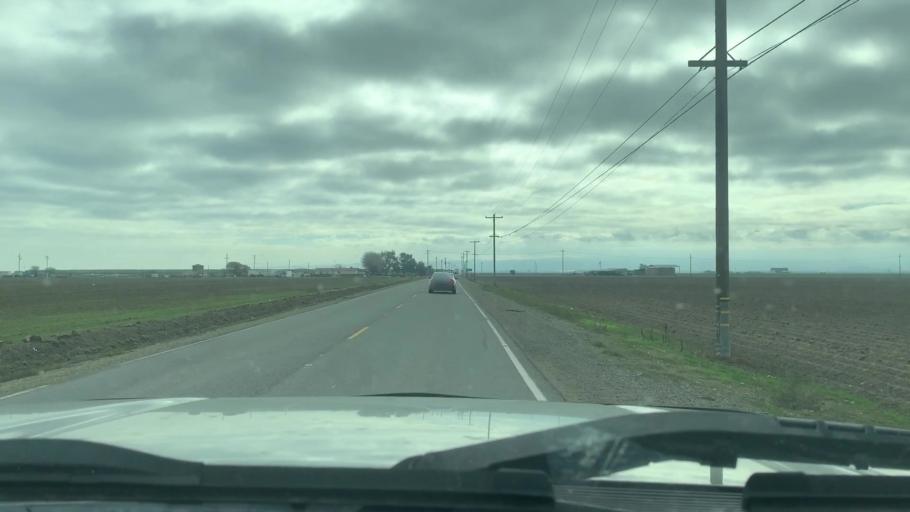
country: US
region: California
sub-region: Merced County
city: Los Banos
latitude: 37.0311
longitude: -120.8360
